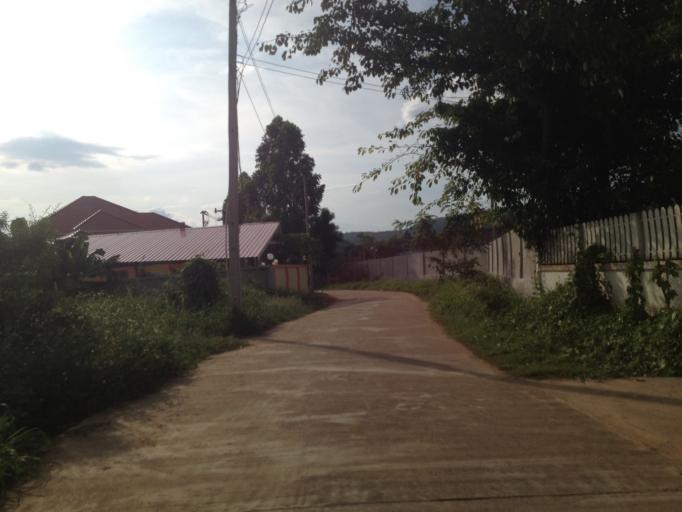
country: TH
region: Chiang Mai
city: Hang Dong
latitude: 18.7136
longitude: 98.9132
